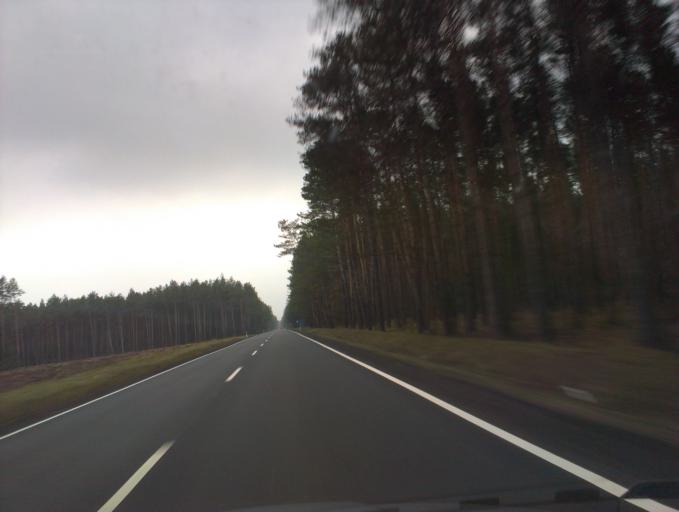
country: PL
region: Greater Poland Voivodeship
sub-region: Powiat zlotowski
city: Tarnowka
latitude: 53.3261
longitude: 16.7951
